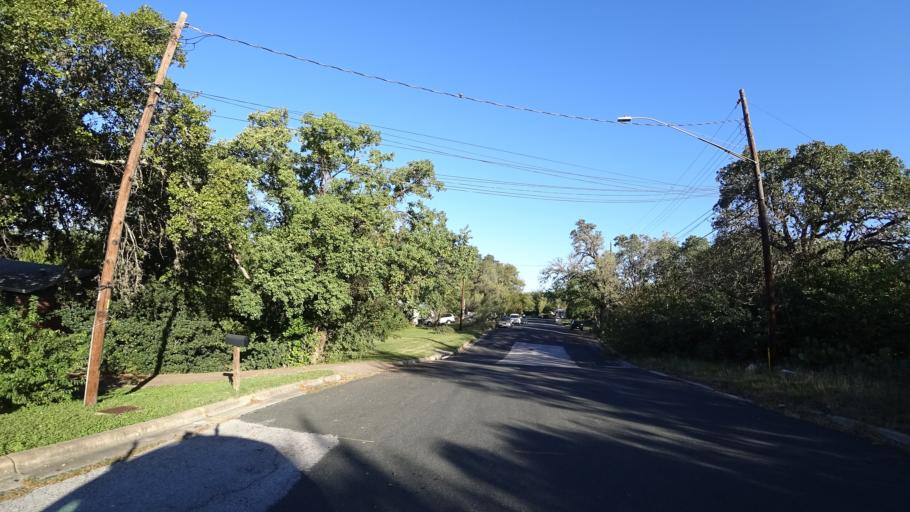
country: US
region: Texas
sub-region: Travis County
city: Austin
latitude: 30.2940
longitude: -97.6864
